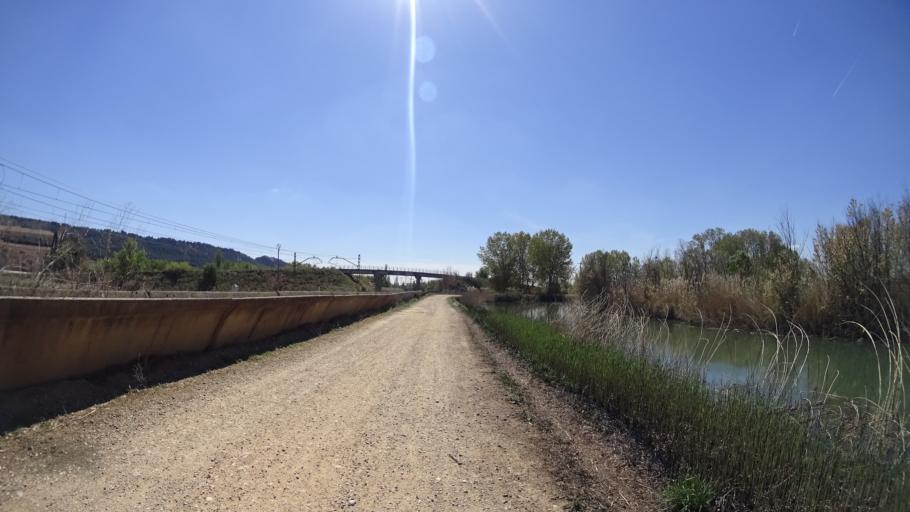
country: ES
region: Castille and Leon
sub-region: Provincia de Valladolid
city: Cabezon
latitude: 41.7544
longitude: -4.6348
